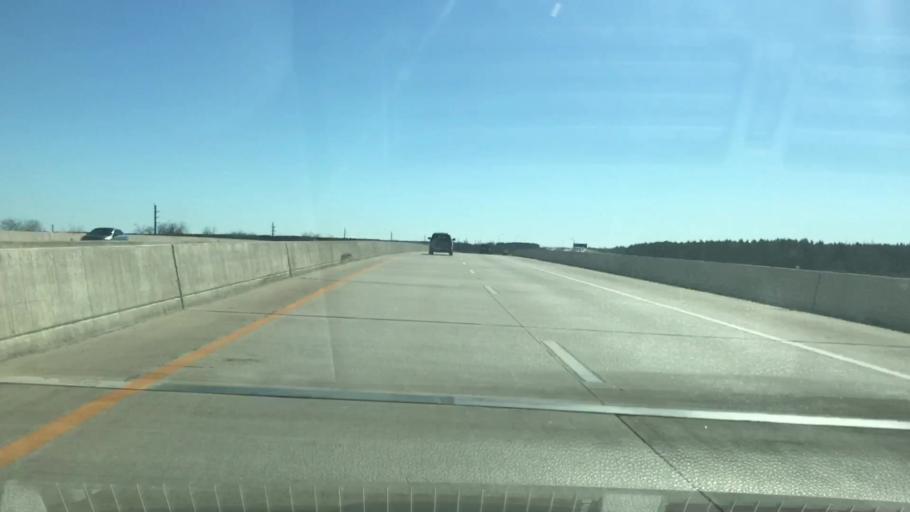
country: US
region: Texas
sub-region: Harris County
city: Cypress
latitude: 29.9048
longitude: -95.7587
